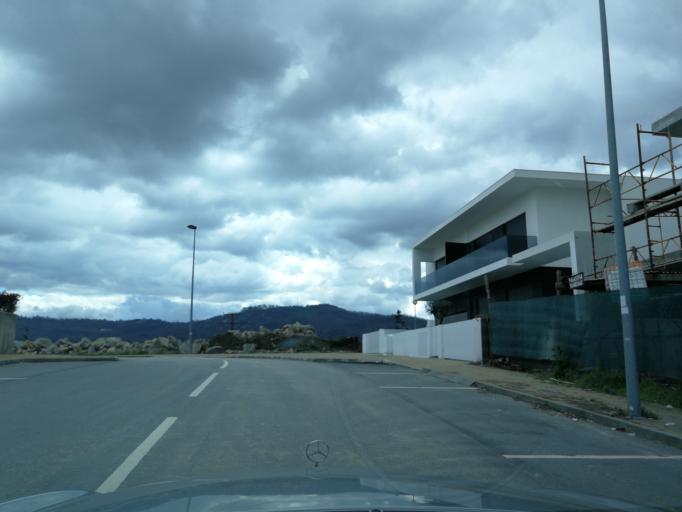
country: PT
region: Braga
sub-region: Braga
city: Braga
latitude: 41.5349
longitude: -8.4255
